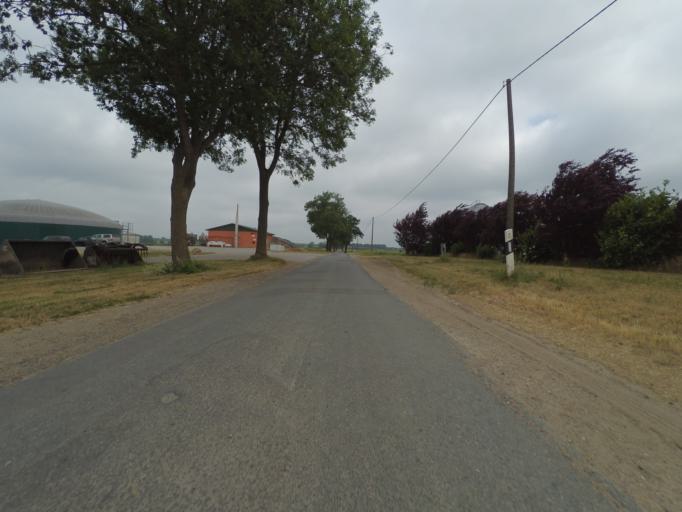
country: DE
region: Mecklenburg-Vorpommern
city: Plau am See
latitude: 53.5224
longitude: 12.2215
